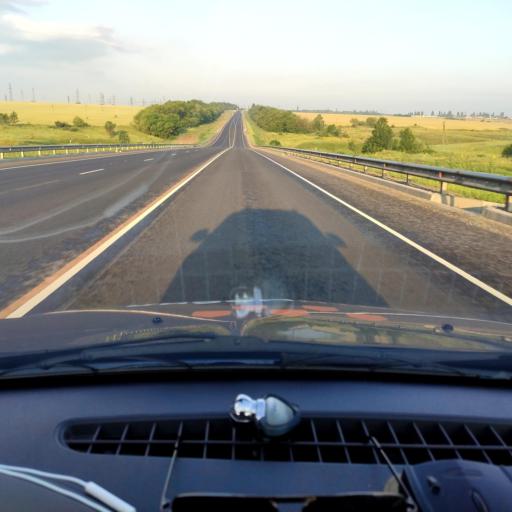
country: RU
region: Lipetsk
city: Yelets
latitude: 52.5807
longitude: 38.5730
